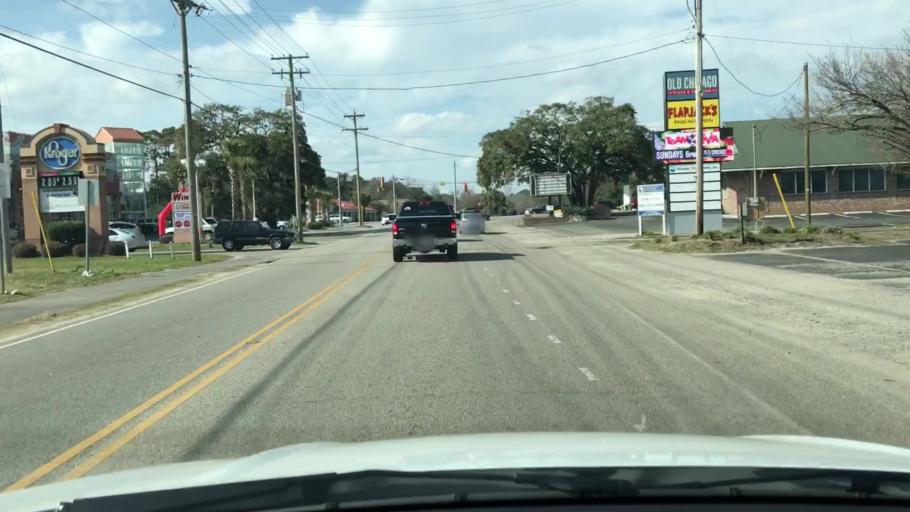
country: US
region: South Carolina
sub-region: Horry County
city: Garden City
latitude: 33.5852
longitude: -79.0112
